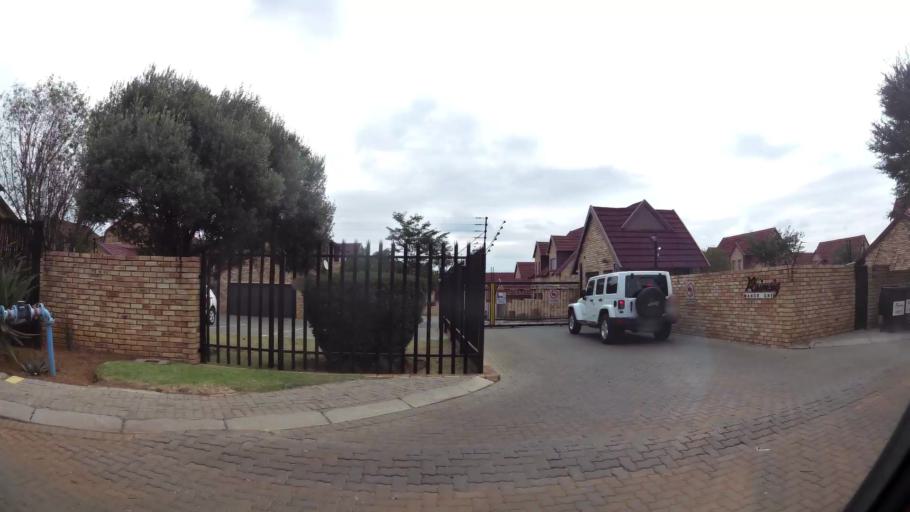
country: ZA
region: Gauteng
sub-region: West Rand District Municipality
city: Muldersdriseloop
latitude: -26.0922
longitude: 27.8778
